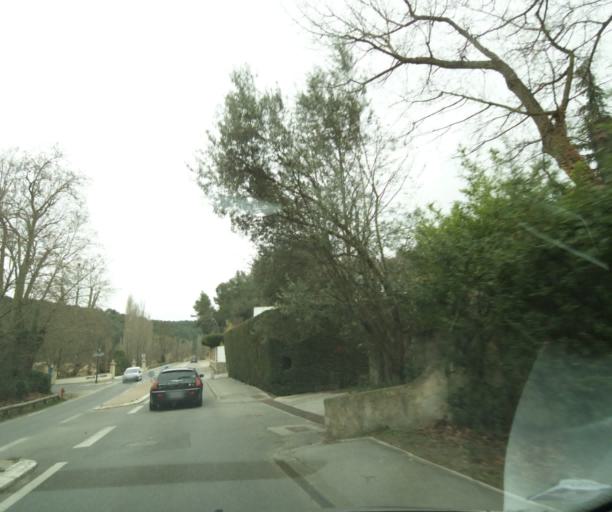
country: FR
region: Provence-Alpes-Cote d'Azur
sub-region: Departement des Bouches-du-Rhone
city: Saint-Marc-Jaumegarde
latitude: 43.5389
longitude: 5.4851
